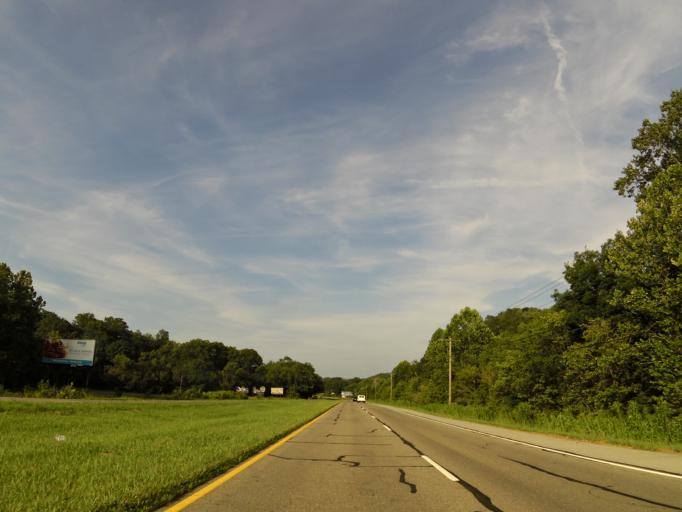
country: US
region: Tennessee
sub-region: Sevier County
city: Sevierville
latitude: 35.8642
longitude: -83.6087
